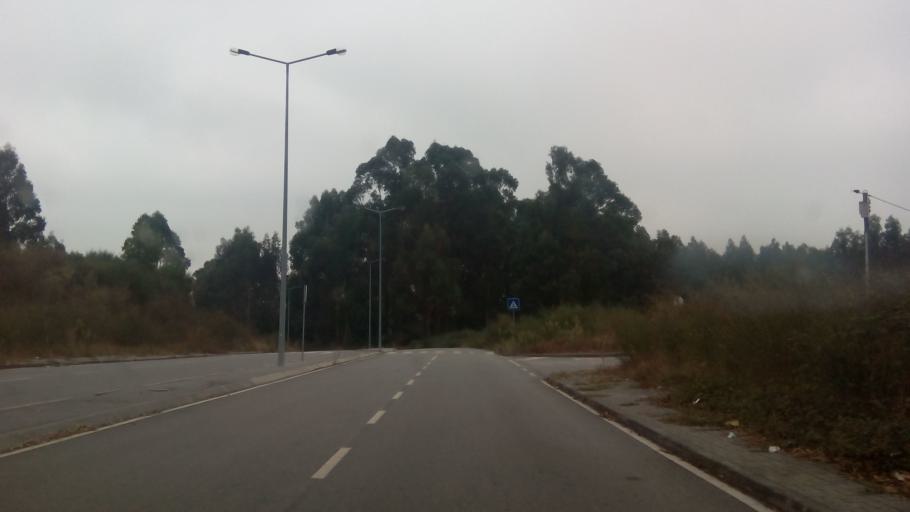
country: PT
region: Porto
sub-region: Paredes
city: Madalena
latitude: 41.2210
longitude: -8.3685
